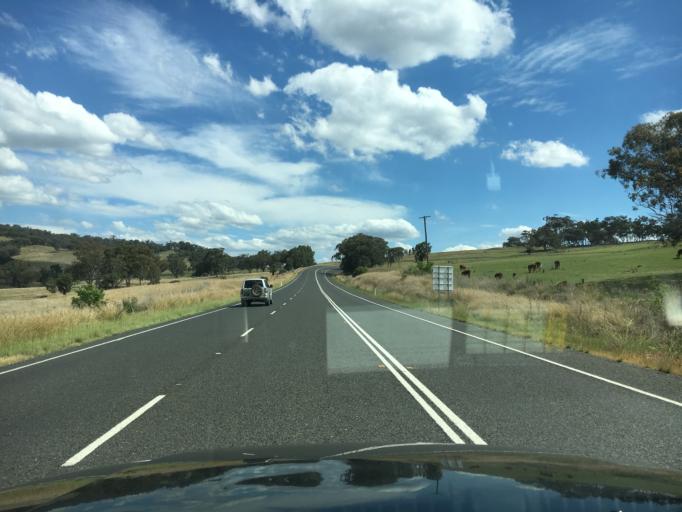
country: AU
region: New South Wales
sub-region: Liverpool Plains
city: Quirindi
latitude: -31.4367
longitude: 150.8816
